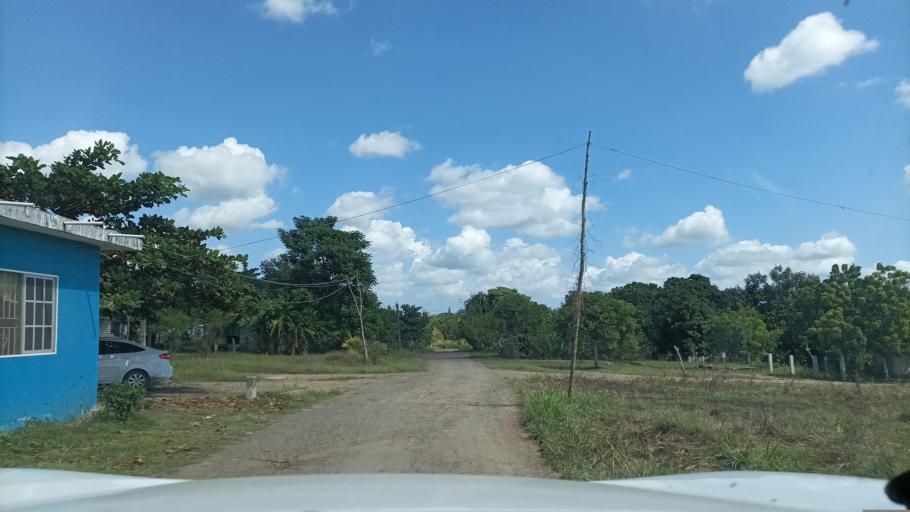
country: MX
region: Veracruz
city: Manlio Fabio Altamirano
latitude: 19.0893
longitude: -96.3413
